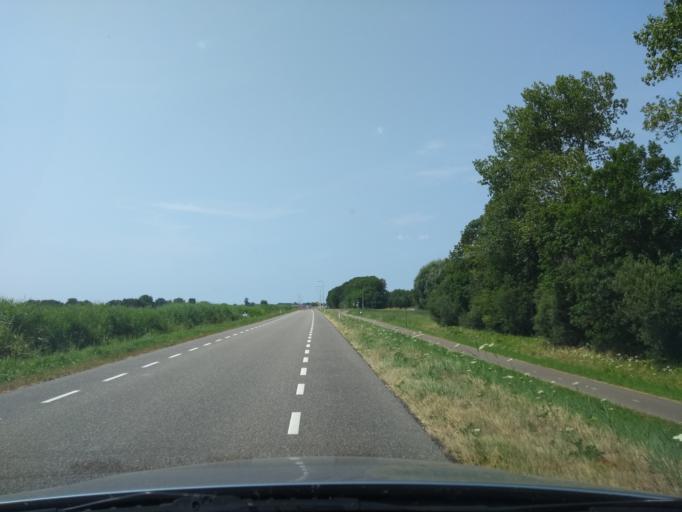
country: NL
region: North Holland
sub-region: Gemeente Langedijk
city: Broek op Langedijk
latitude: 52.6341
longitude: 4.8180
